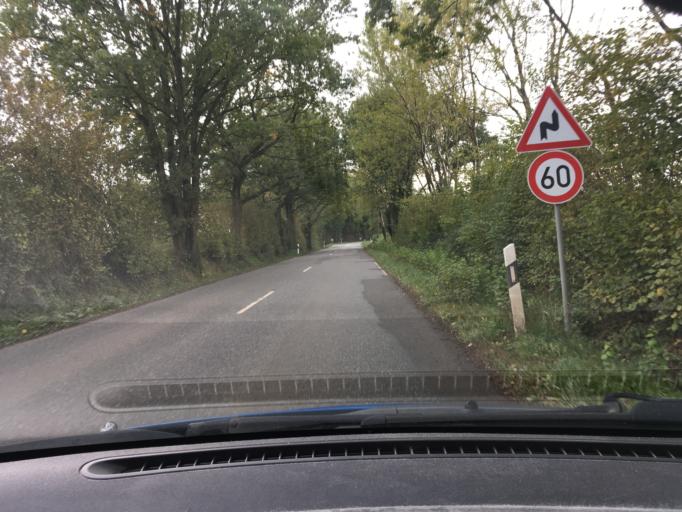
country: DE
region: Schleswig-Holstein
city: Klein Ronnau
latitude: 53.9818
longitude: 10.3119
